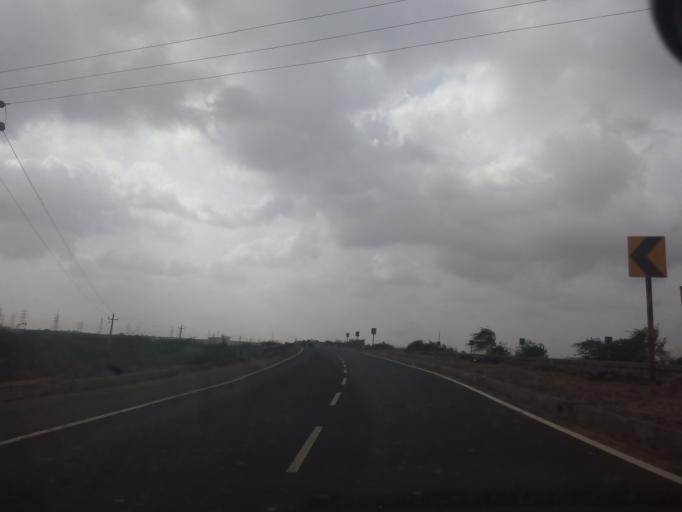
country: IN
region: Gujarat
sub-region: Rajkot
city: Morbi
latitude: 23.1339
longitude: 70.7534
